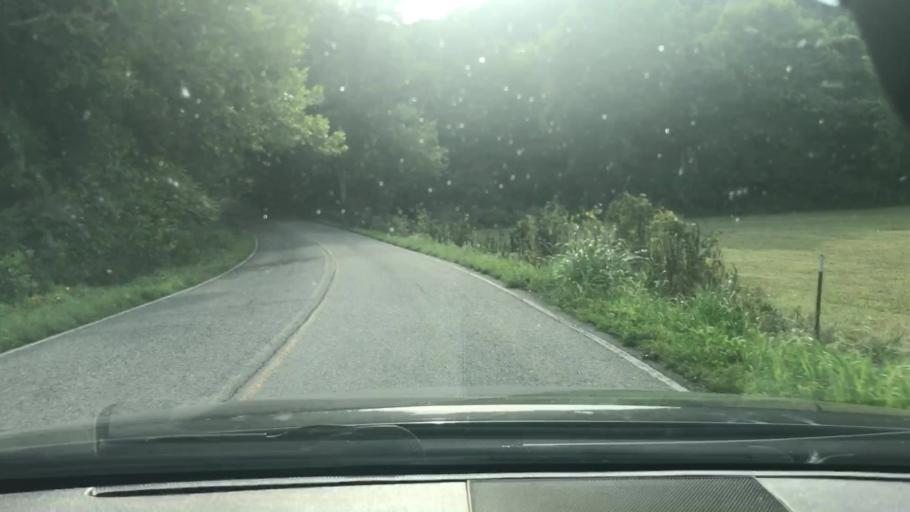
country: US
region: Tennessee
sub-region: Dickson County
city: Charlotte
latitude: 36.1797
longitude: -87.2725
